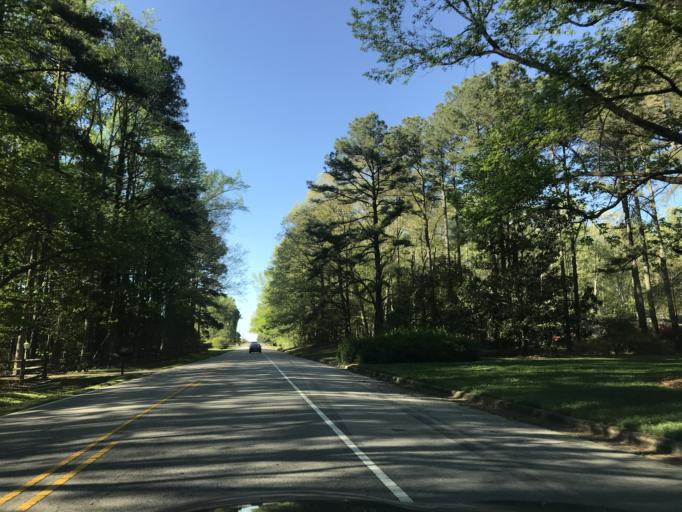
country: US
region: North Carolina
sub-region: Wake County
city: Knightdale
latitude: 35.8287
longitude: -78.5555
